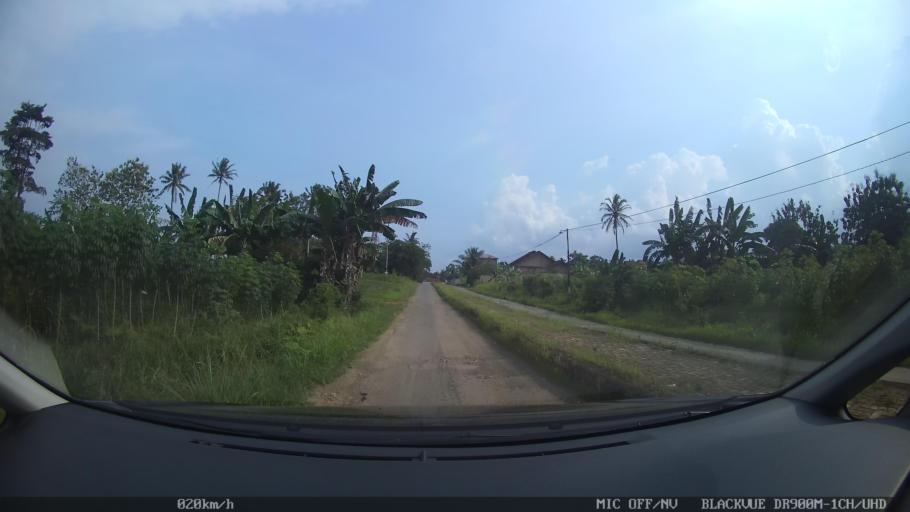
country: ID
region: Lampung
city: Kedaton
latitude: -5.3631
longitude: 105.2139
